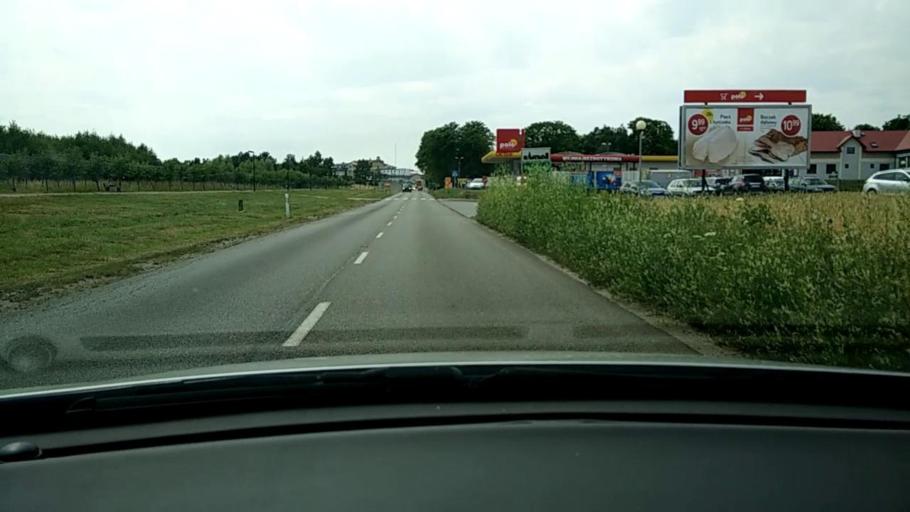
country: PL
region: Pomeranian Voivodeship
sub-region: Powiat pucki
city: Kosakowo
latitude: 54.5914
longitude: 18.4976
